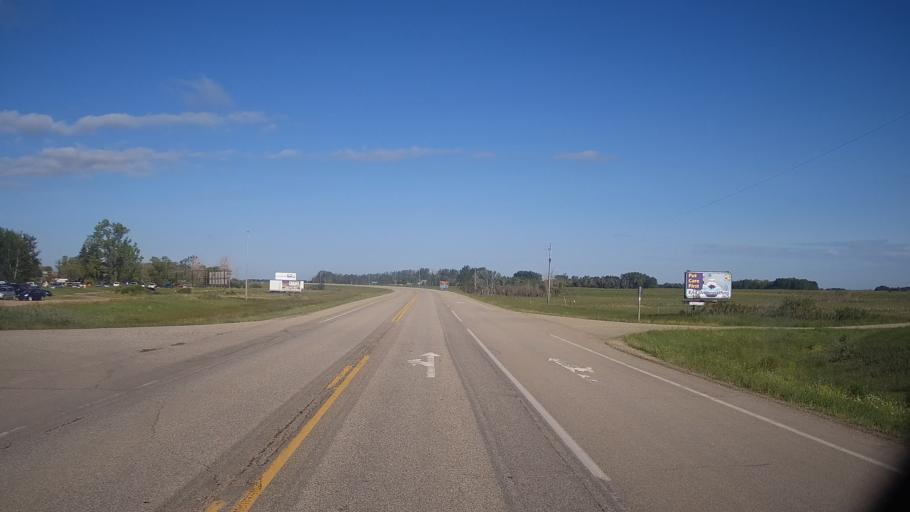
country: CA
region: Saskatchewan
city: Lanigan
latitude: 51.8737
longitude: -105.1810
